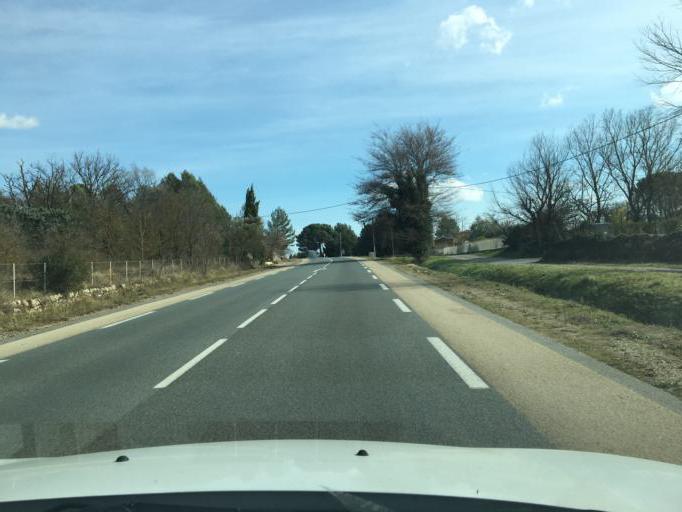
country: FR
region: Provence-Alpes-Cote d'Azur
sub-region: Departement du Var
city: Flayosc
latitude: 43.5310
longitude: 6.4151
